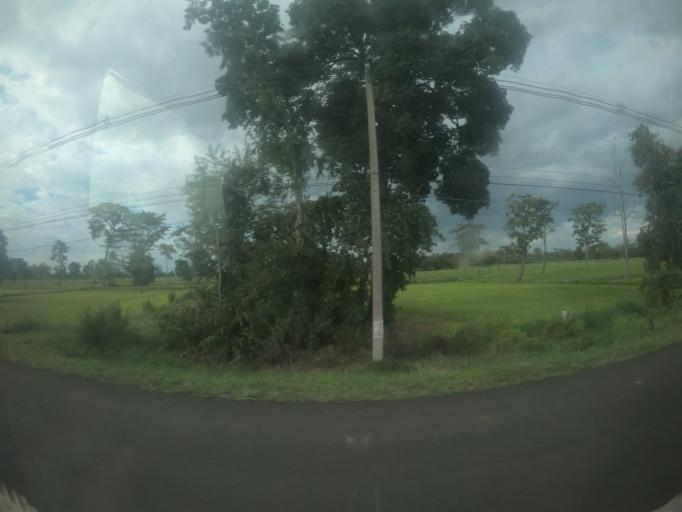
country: TH
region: Surin
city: Kap Choeng
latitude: 14.5393
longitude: 103.5218
